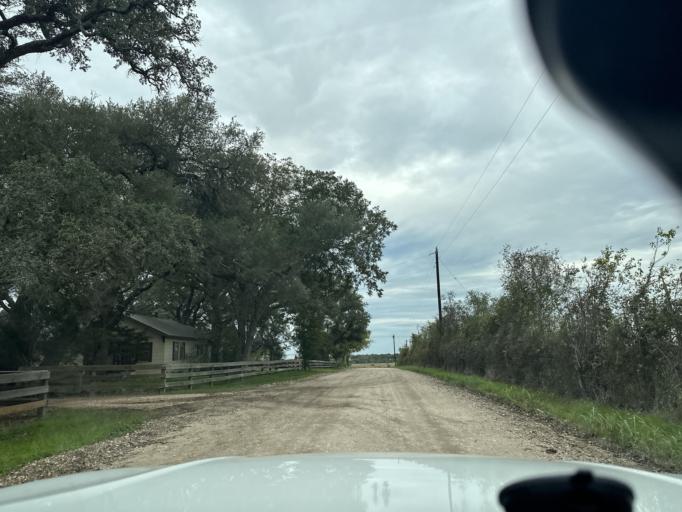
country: US
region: Texas
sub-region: Burleson County
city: Somerville
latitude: 30.1643
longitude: -96.6459
